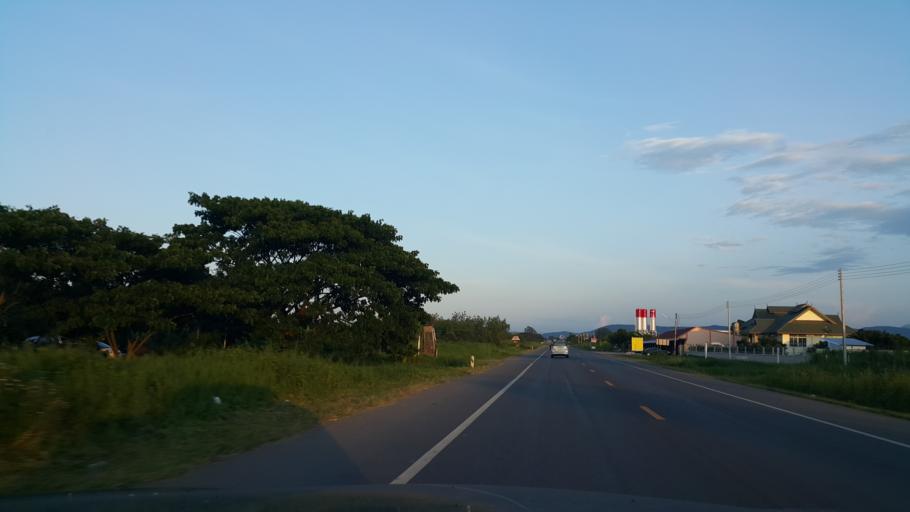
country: TH
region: Lamphun
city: Pa Sang
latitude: 18.4885
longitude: 98.9243
